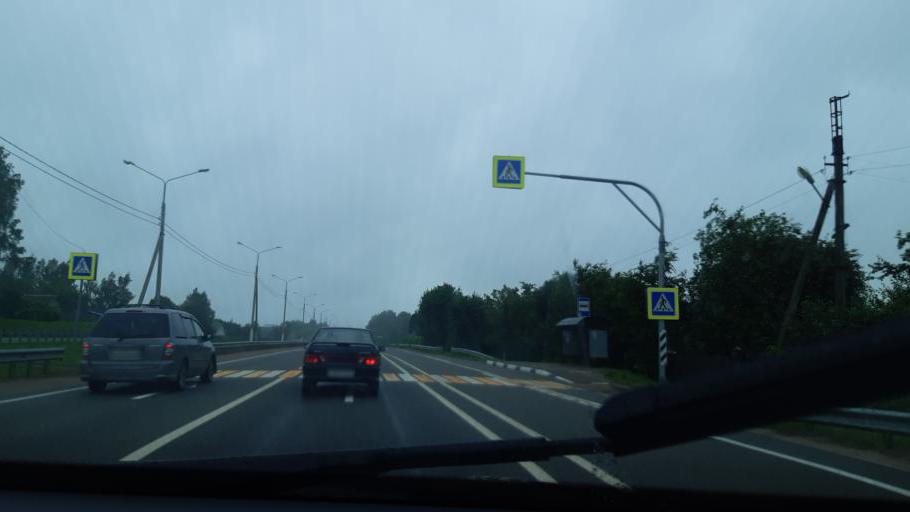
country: RU
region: Smolensk
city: Talashkino
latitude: 54.6734
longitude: 32.1474
